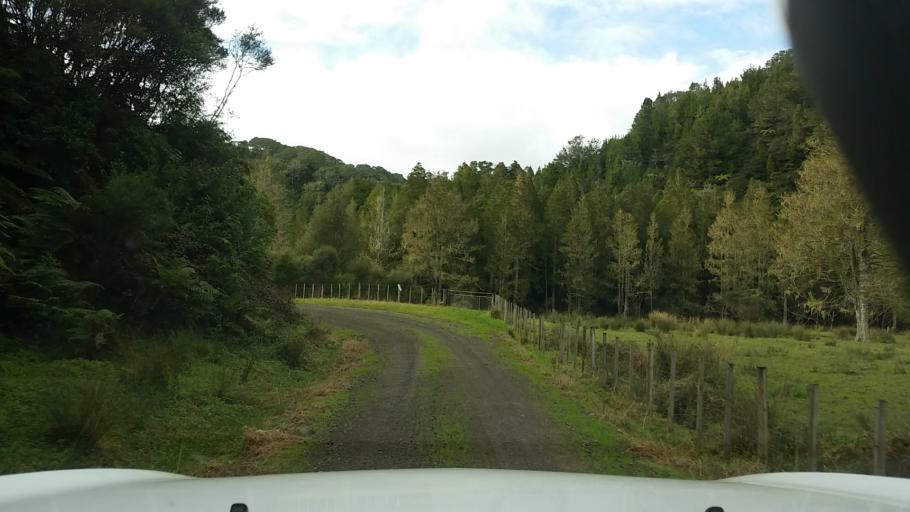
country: NZ
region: Taranaki
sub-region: New Plymouth District
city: Waitara
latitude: -38.8134
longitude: 174.6245
